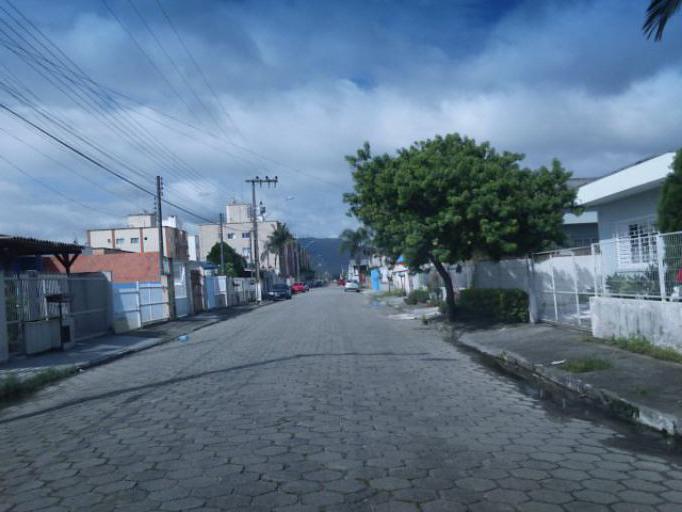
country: BR
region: Santa Catarina
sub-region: Itapema
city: Itapema
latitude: -27.1245
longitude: -48.6170
